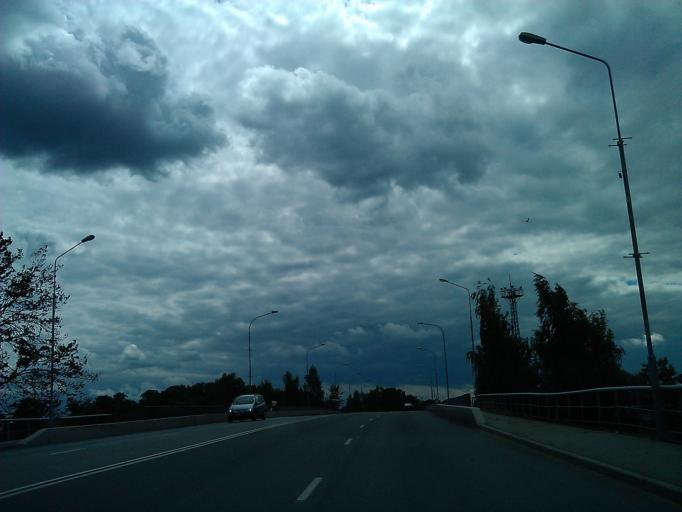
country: LV
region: Jelgava
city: Jelgava
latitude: 56.6399
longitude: 23.7291
